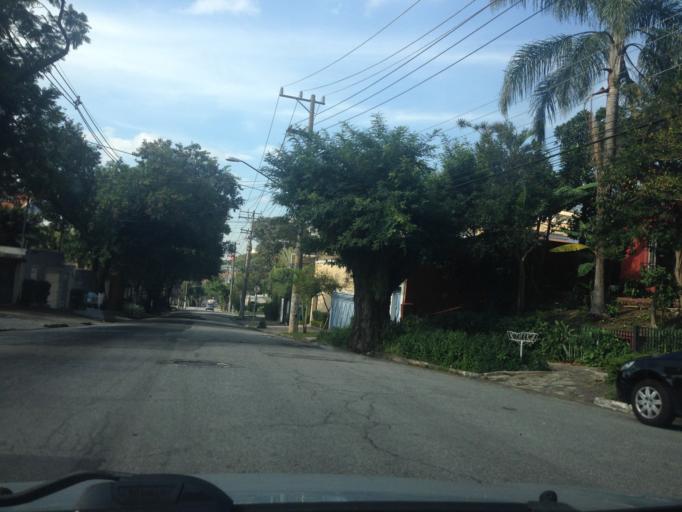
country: BR
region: Sao Paulo
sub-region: Osasco
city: Osasco
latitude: -23.5211
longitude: -46.7143
